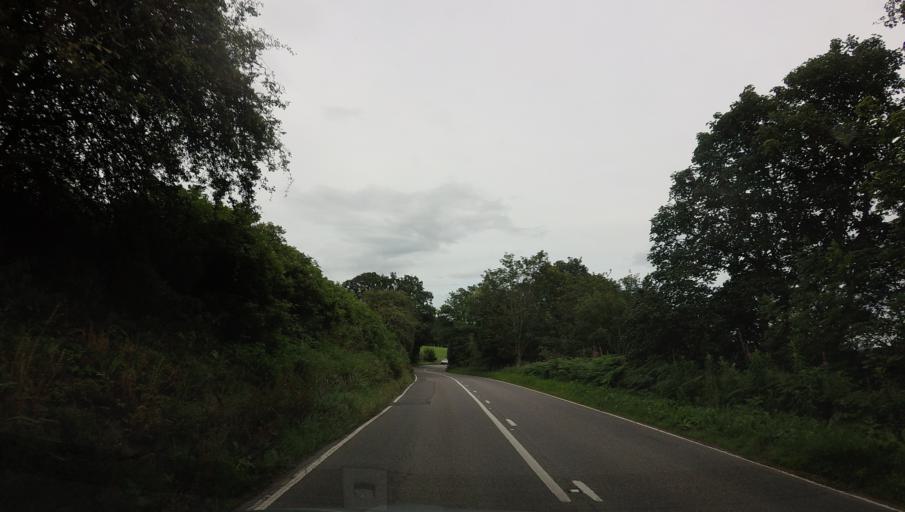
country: GB
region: Scotland
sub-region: Aberdeenshire
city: Torphins
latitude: 57.0895
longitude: -2.6951
